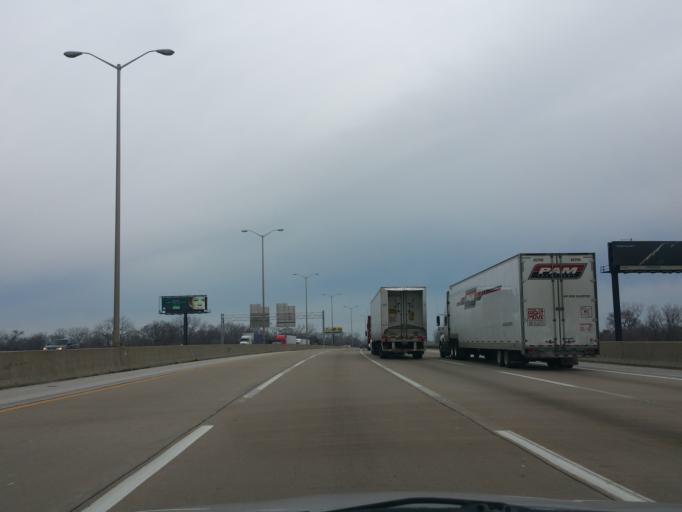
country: US
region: Illinois
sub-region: Cook County
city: Midlothian
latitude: 41.6392
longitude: -87.7183
